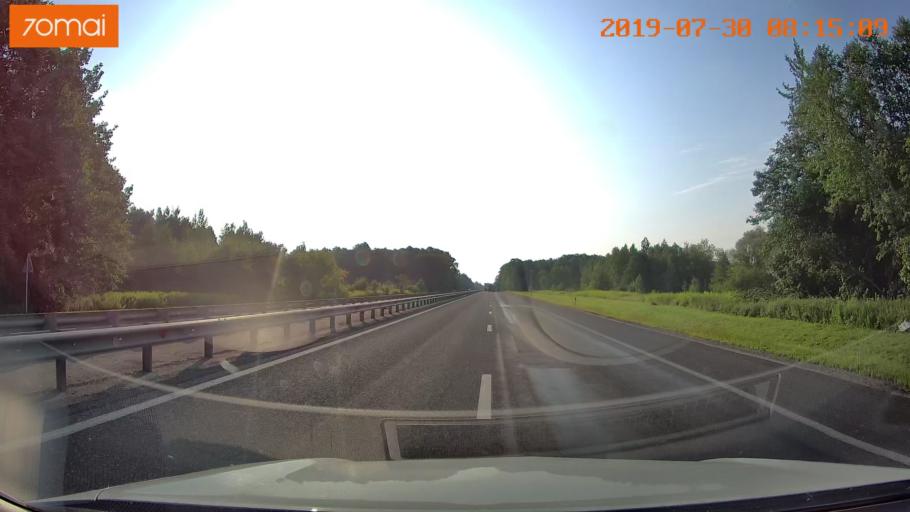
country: RU
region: Kaliningrad
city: Zheleznodorozhnyy
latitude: 54.6451
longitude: 21.3773
